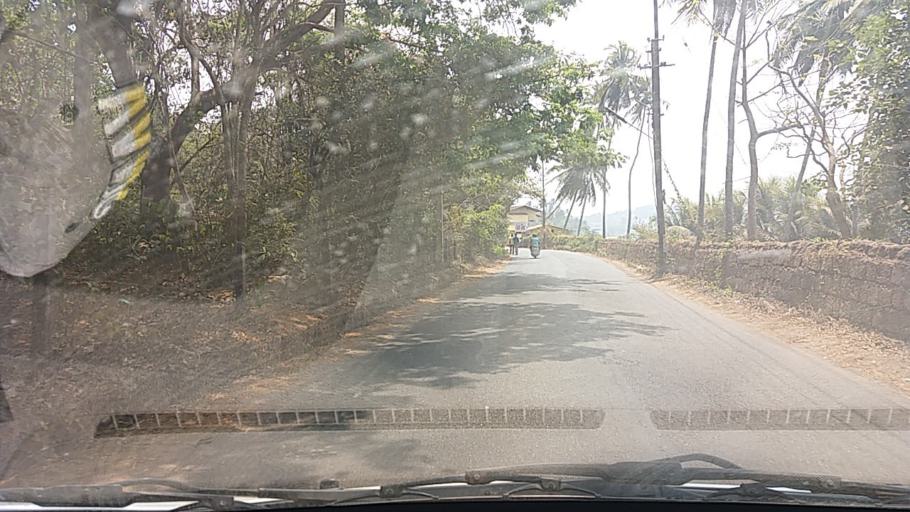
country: IN
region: Goa
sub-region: North Goa
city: Panaji
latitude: 15.5103
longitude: 73.8213
